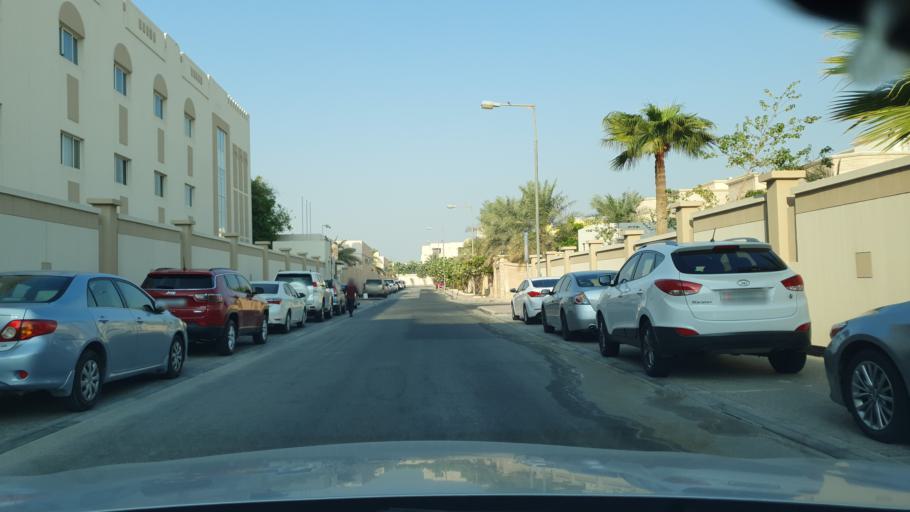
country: BH
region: Northern
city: Madinat `Isa
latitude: 26.1534
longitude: 50.5411
